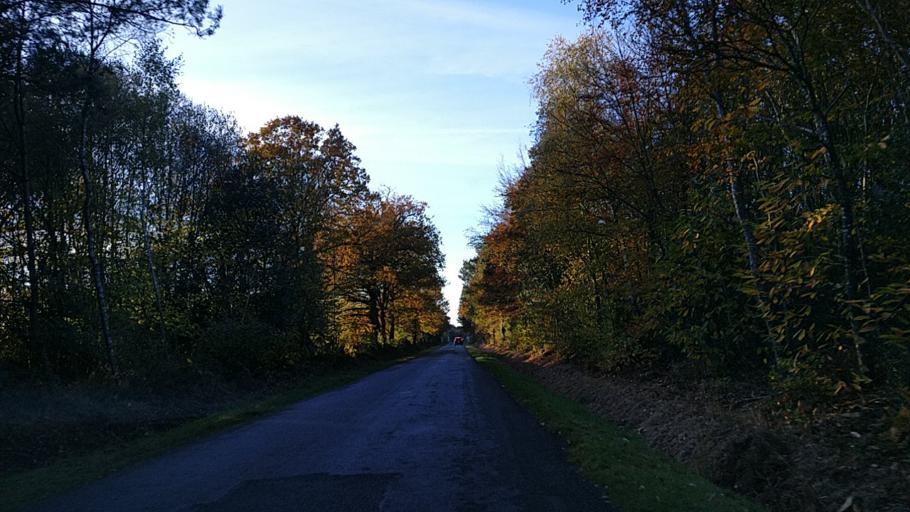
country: FR
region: Brittany
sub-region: Departement d'Ille-et-Vilaine
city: Saint-Sulpice-la-Foret
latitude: 48.1937
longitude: -1.5713
